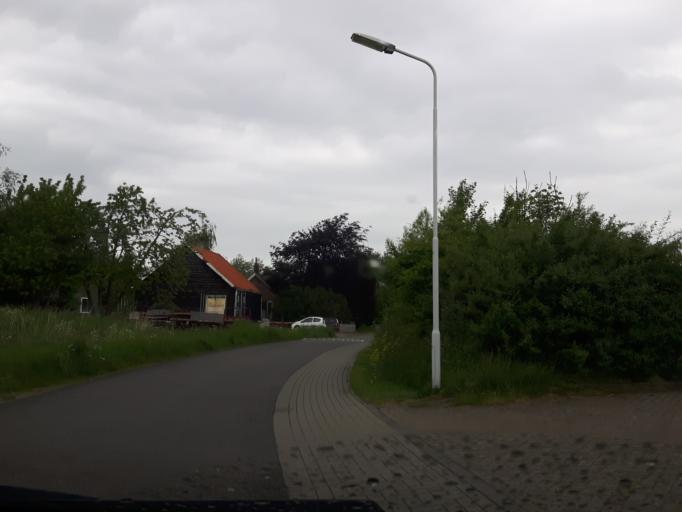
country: NL
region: Zeeland
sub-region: Gemeente Goes
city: Goes
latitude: 51.4991
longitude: 3.8612
